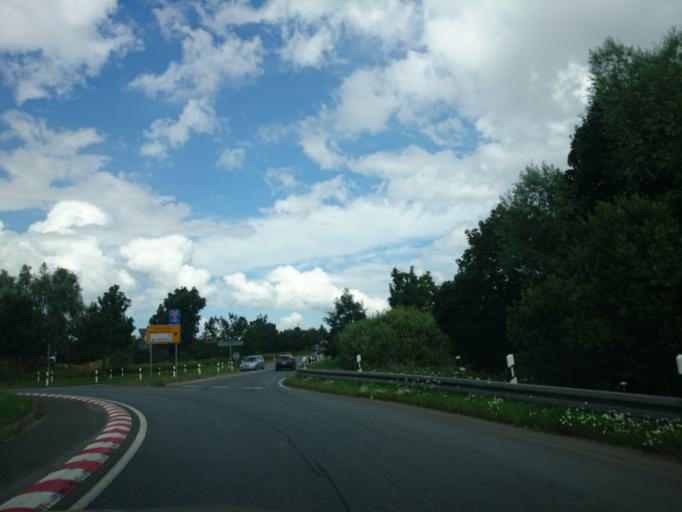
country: DE
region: Mecklenburg-Vorpommern
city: Wismar
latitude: 53.8709
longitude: 11.4495
